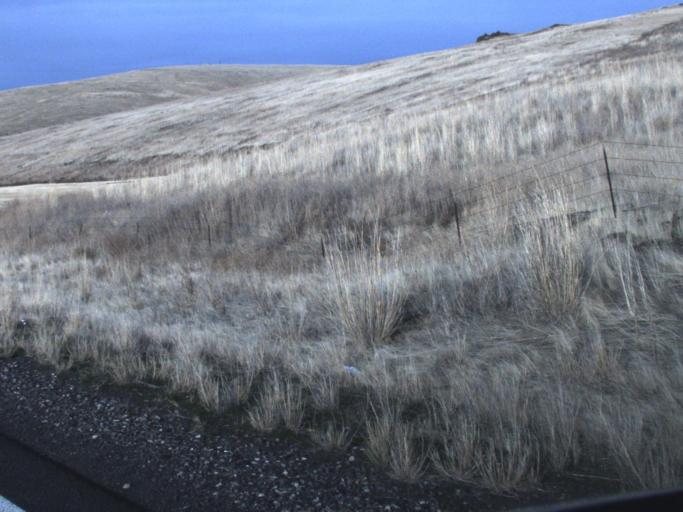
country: US
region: Washington
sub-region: Garfield County
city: Pomeroy
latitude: 46.5087
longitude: -117.7850
